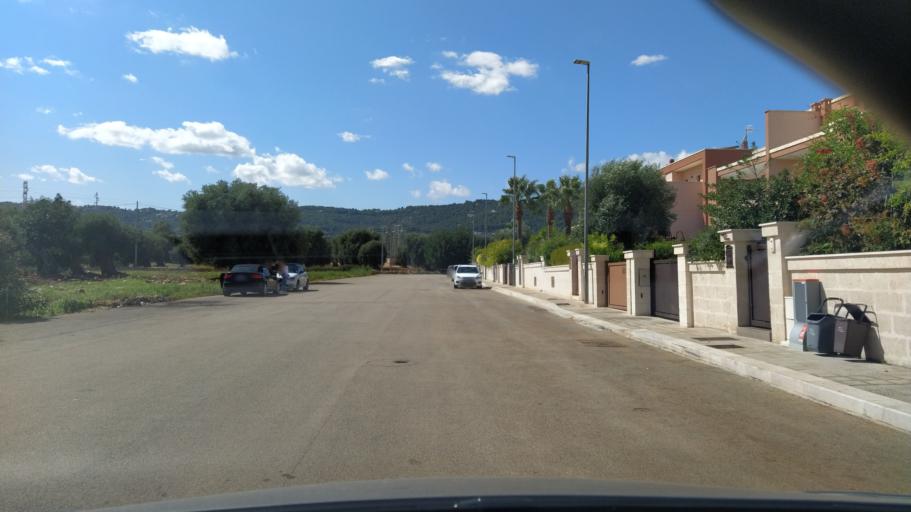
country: IT
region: Apulia
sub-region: Provincia di Brindisi
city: Fasano
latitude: 40.8267
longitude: 17.3642
